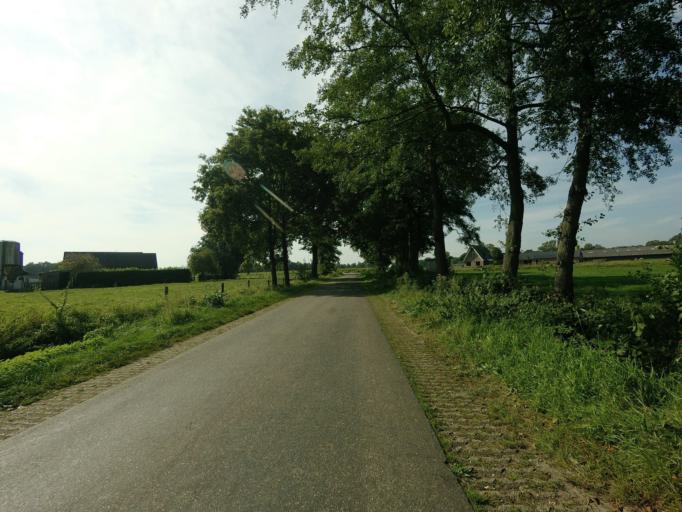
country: NL
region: Overijssel
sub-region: Gemeente Hof van Twente
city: Goor
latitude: 52.2559
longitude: 6.6038
